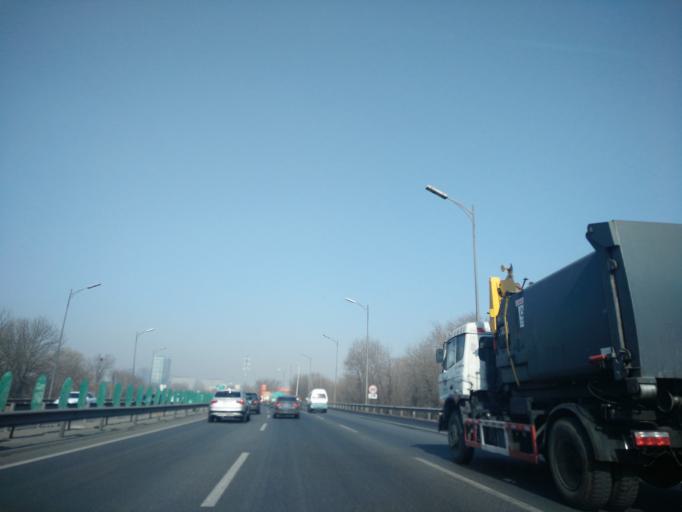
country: CN
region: Beijing
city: Wangjing
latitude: 40.0101
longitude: 116.4820
